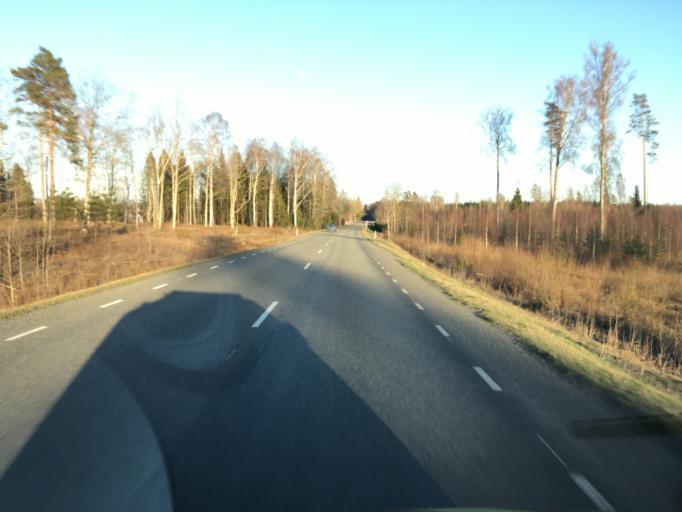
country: EE
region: Raplamaa
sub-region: Rapla vald
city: Rapla
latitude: 59.0699
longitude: 24.9085
